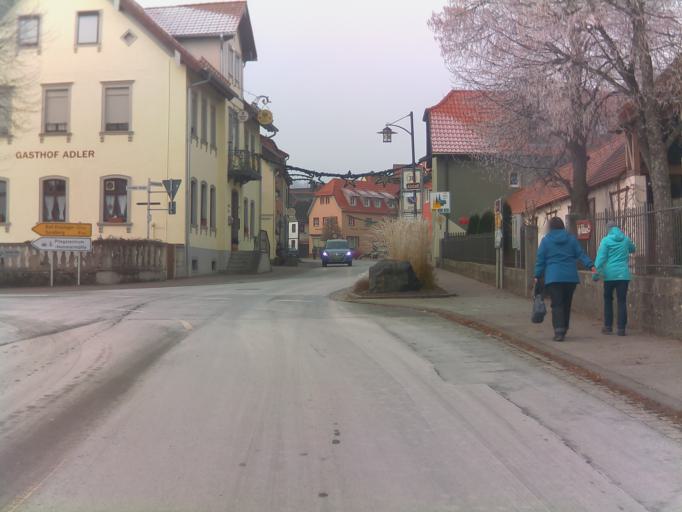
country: DE
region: Bavaria
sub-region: Regierungsbezirk Unterfranken
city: Bischofsheim an der Rhon
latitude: 50.4007
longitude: 10.0109
